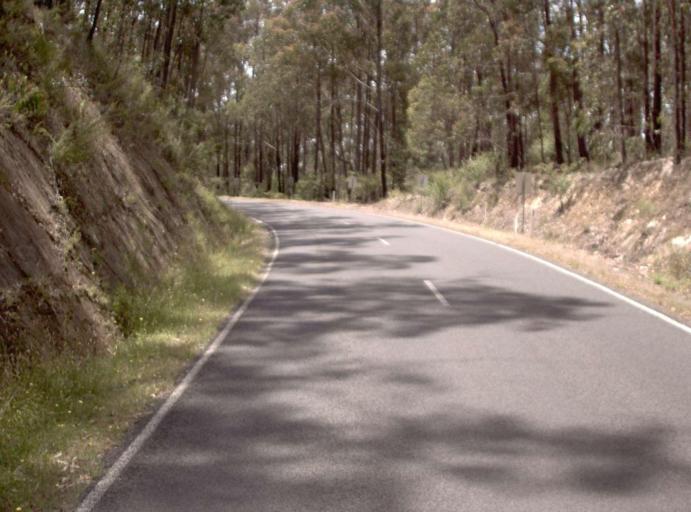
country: AU
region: Victoria
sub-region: Latrobe
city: Moe
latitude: -38.0345
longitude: 146.3464
